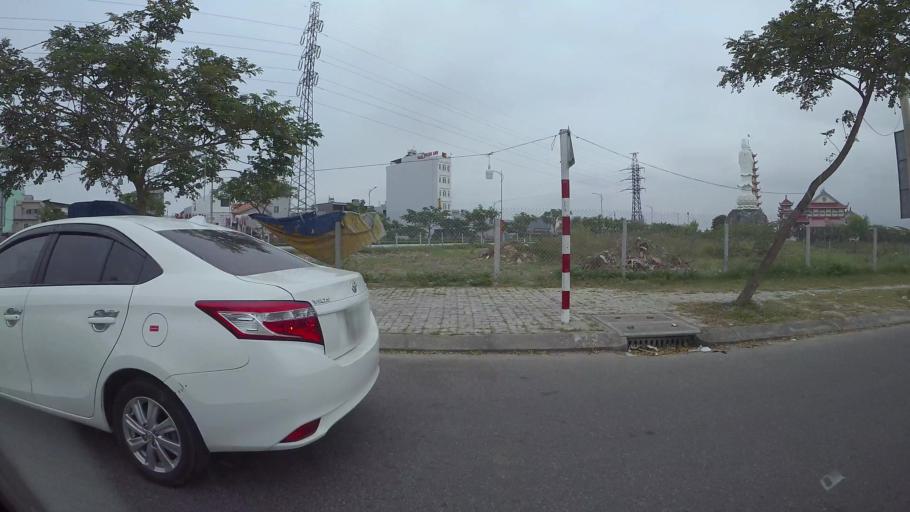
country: VN
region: Da Nang
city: Lien Chieu
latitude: 16.0667
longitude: 108.1711
